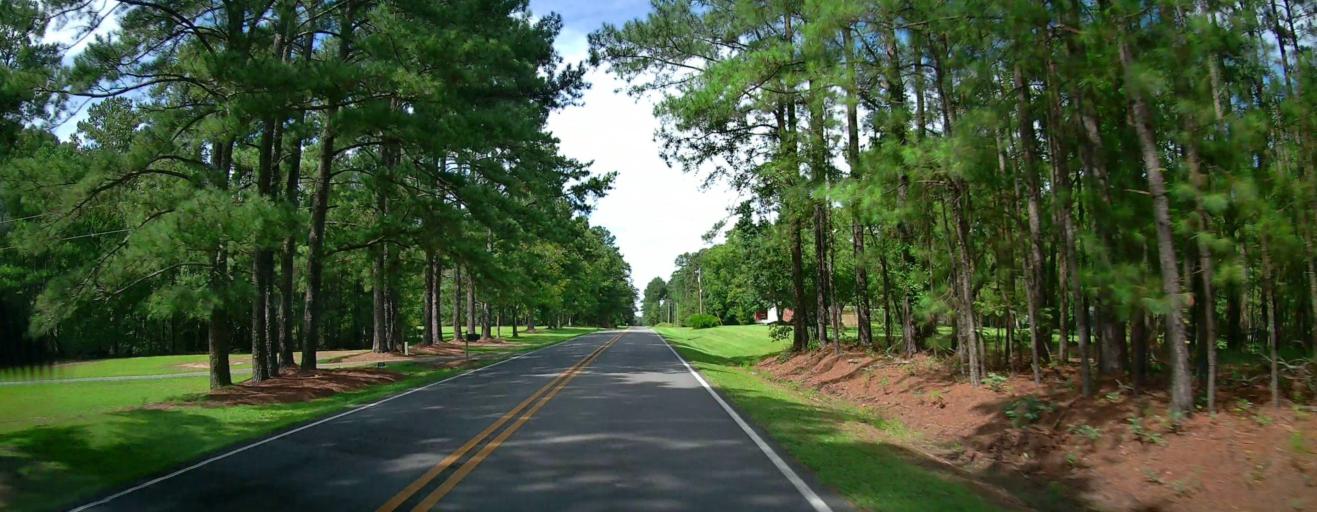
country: US
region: Georgia
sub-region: Taylor County
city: Butler
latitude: 32.5037
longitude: -84.2025
